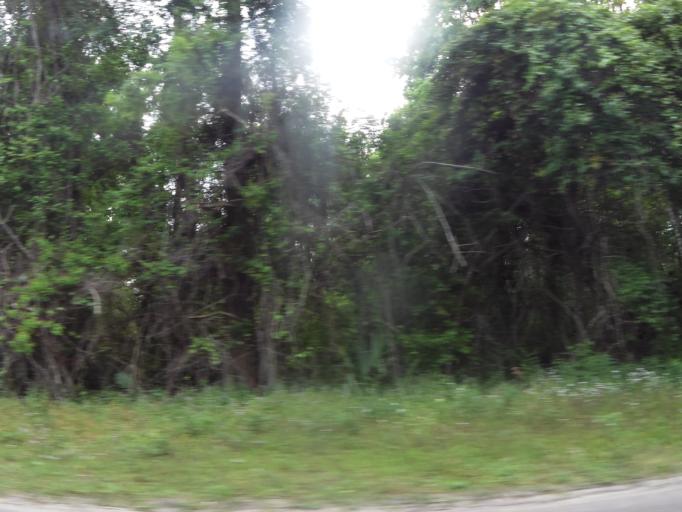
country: US
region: Florida
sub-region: Nassau County
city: Hilliard
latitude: 30.6935
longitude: -81.9244
